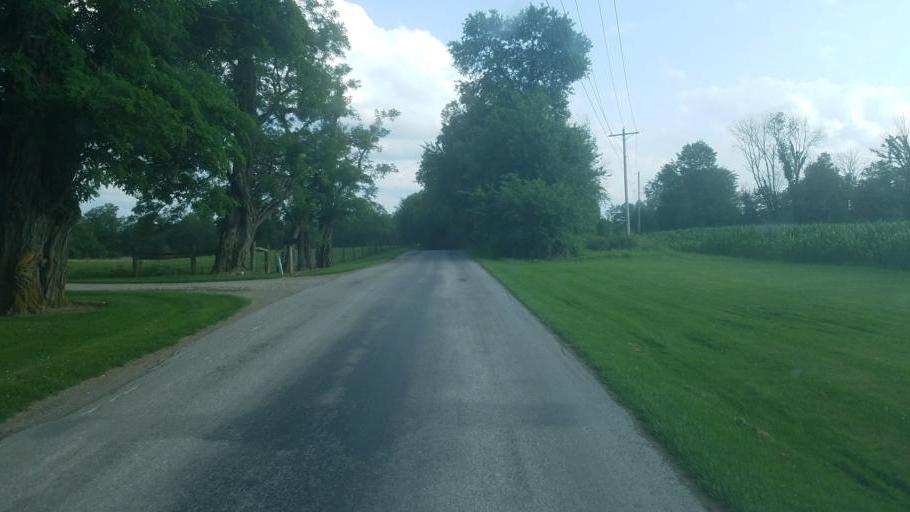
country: US
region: Ohio
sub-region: Knox County
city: Fredericktown
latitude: 40.5307
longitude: -82.6333
